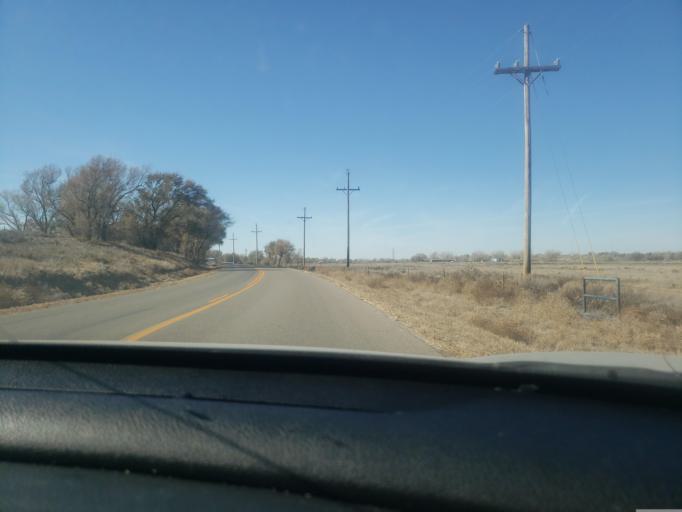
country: US
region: Kansas
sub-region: Finney County
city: Garden City
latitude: 37.9516
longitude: -100.8599
